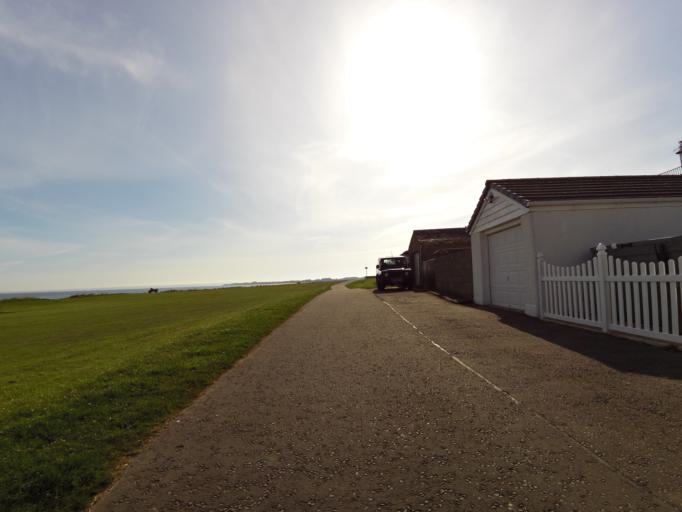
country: GB
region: Scotland
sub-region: Angus
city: Carnoustie
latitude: 56.5017
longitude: -2.6970
